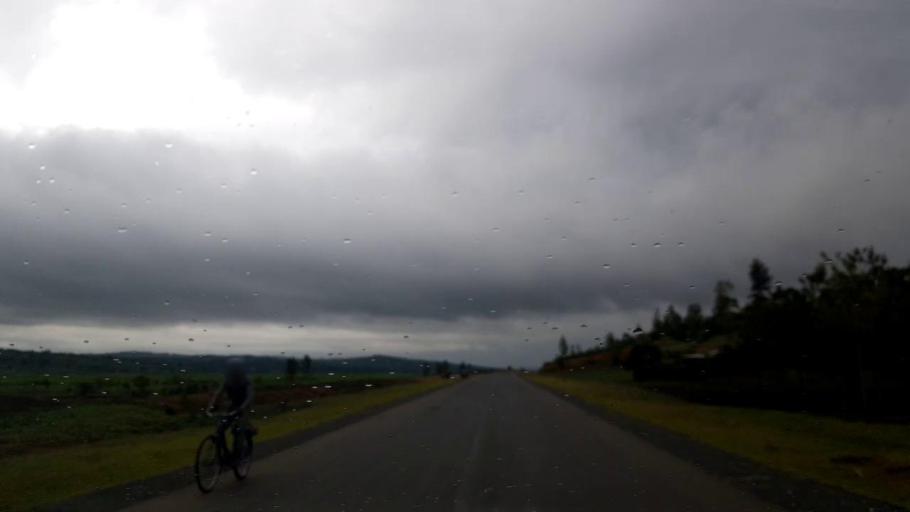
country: RW
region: Northern Province
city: Byumba
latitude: -1.4463
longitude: 30.2495
